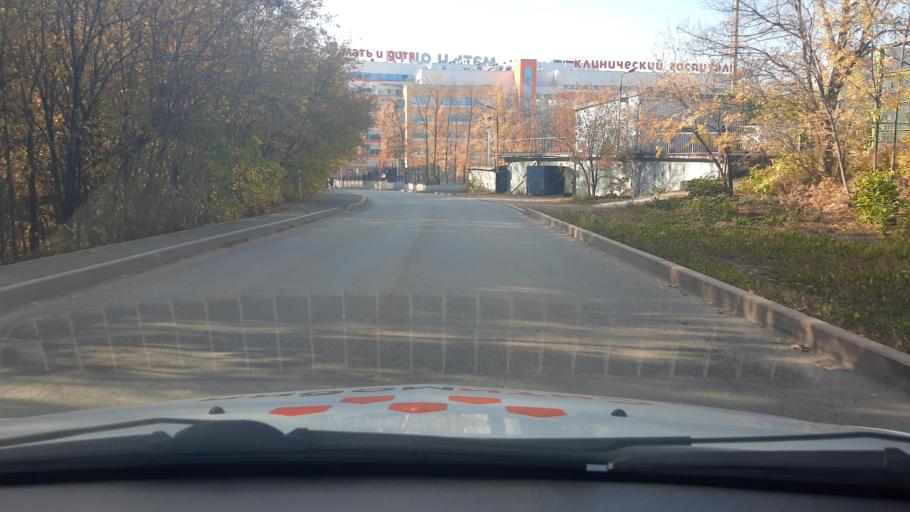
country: RU
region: Bashkortostan
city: Ufa
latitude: 54.7371
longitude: 56.0237
